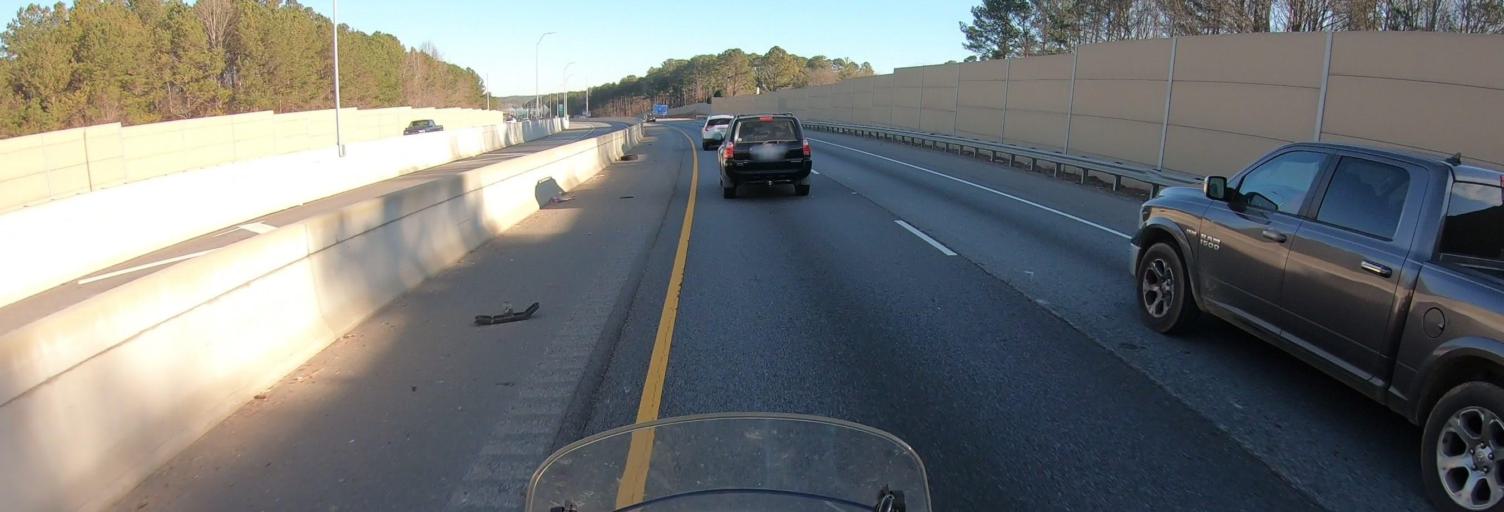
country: US
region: Georgia
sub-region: Cherokee County
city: Woodstock
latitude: 34.0580
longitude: -84.5450
